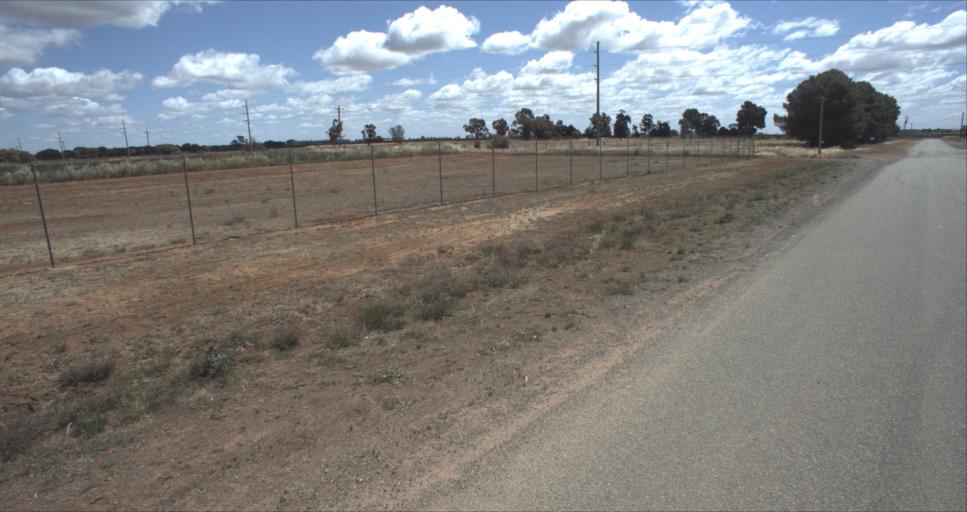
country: AU
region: New South Wales
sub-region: Murrumbidgee Shire
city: Darlington Point
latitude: -34.5128
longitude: 146.1844
